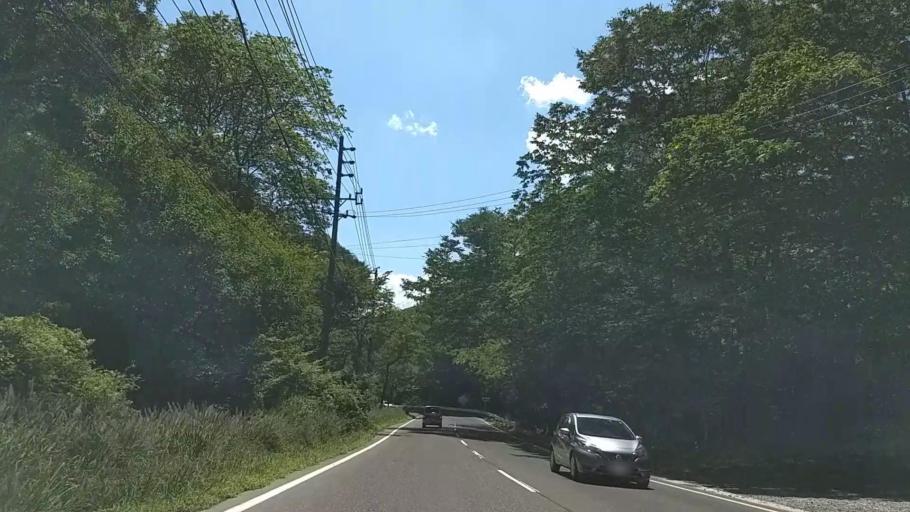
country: JP
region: Nagano
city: Chino
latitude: 36.0651
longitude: 138.2225
